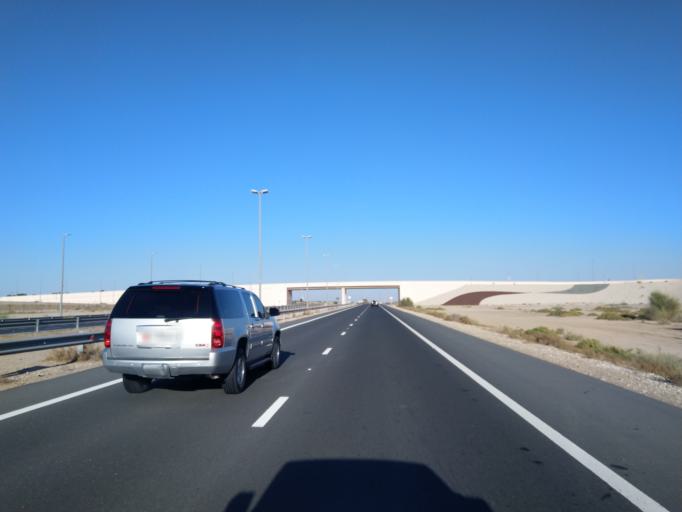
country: OM
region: Al Buraimi
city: Al Buraymi
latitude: 24.5154
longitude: 55.4961
